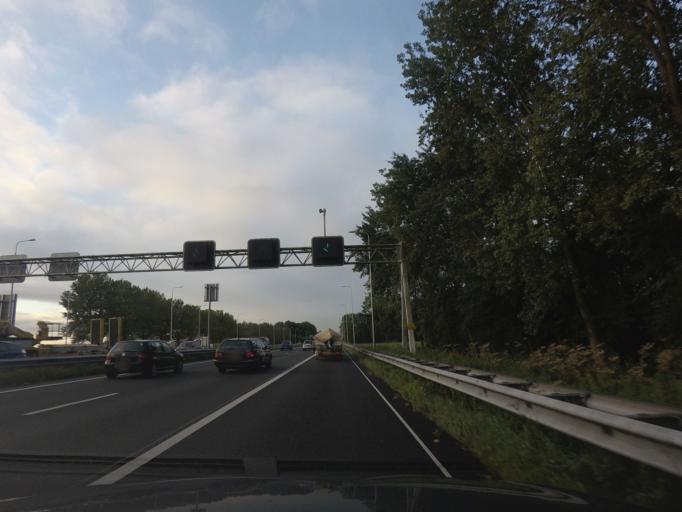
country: NL
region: North Holland
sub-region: Gemeente Uitgeest
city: Uitgeest
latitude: 52.5472
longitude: 4.7196
